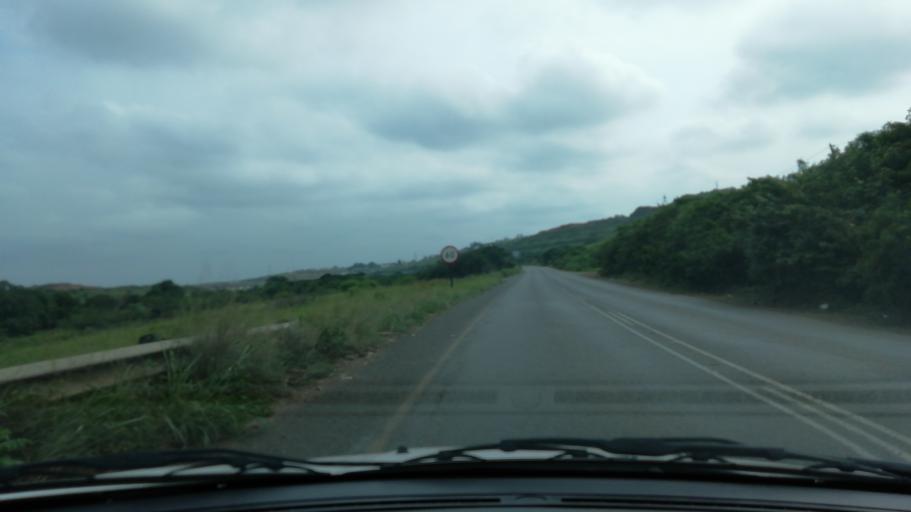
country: ZA
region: KwaZulu-Natal
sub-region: uThungulu District Municipality
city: Empangeni
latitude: -28.7495
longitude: 31.8796
